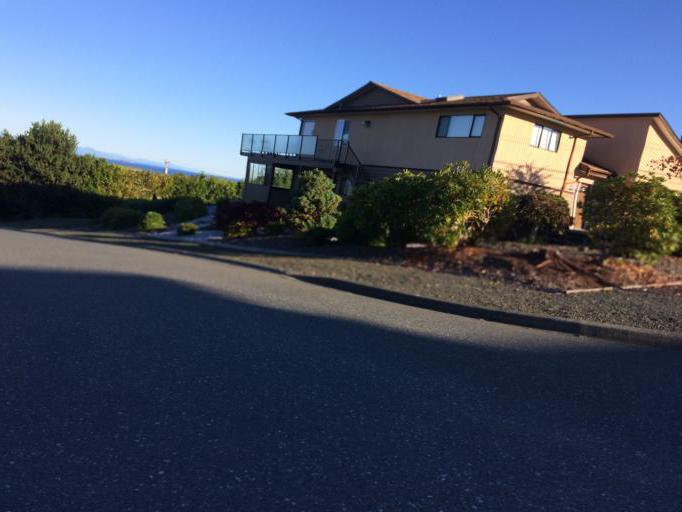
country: CA
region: British Columbia
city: Campbell River
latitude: 49.9977
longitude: -125.2352
